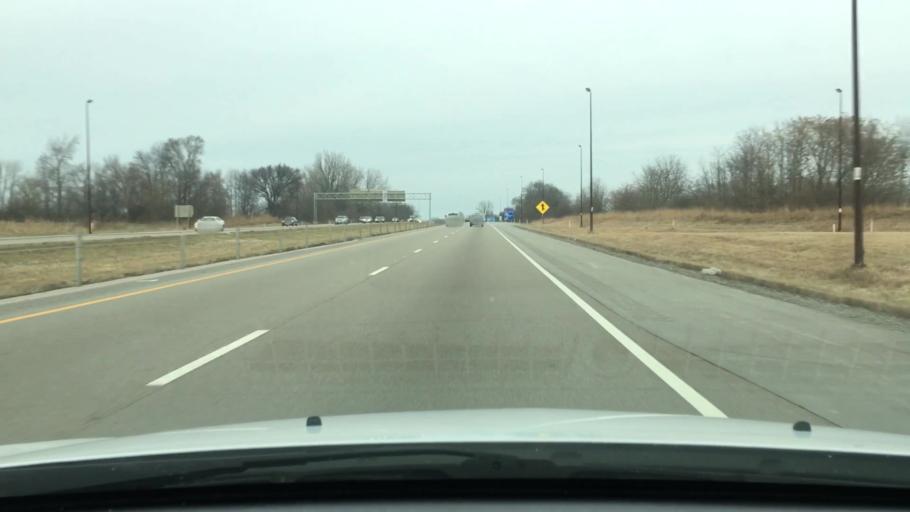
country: US
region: Illinois
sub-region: Sangamon County
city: Grandview
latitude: 39.8036
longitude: -89.5946
